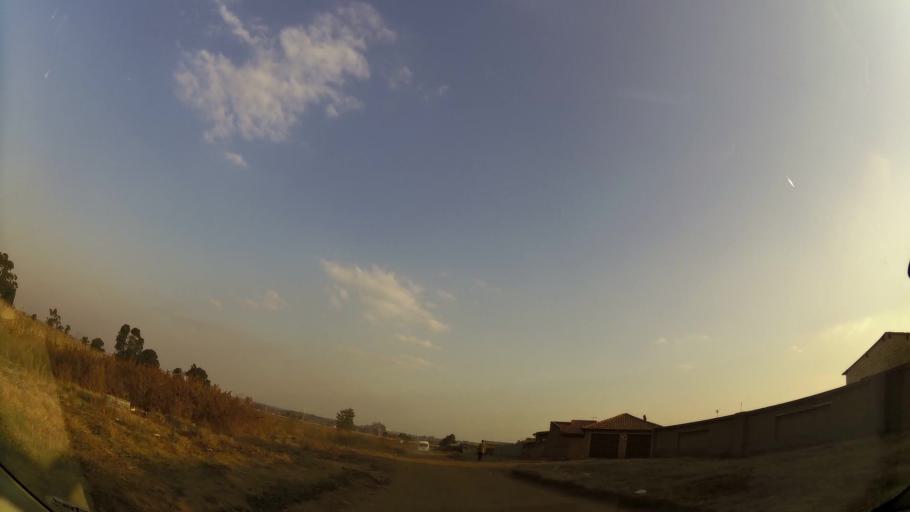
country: ZA
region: Gauteng
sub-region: Ekurhuleni Metropolitan Municipality
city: Benoni
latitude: -26.1614
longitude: 28.3827
